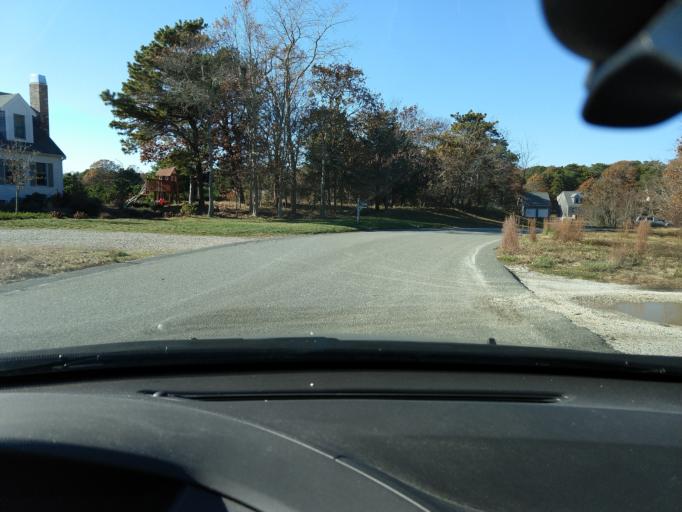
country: US
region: Massachusetts
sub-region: Barnstable County
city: North Eastham
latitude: 41.8731
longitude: -69.9918
